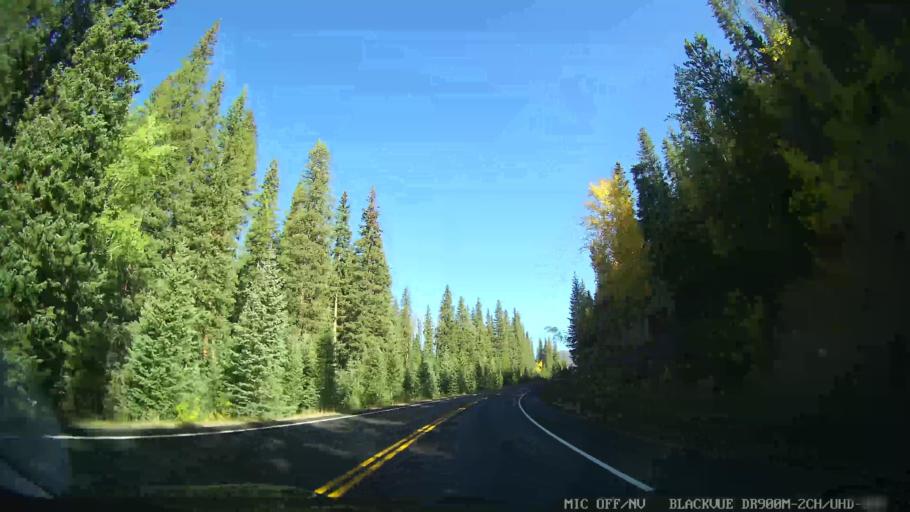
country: US
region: Colorado
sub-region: Grand County
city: Granby
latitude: 40.2994
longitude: -105.8429
